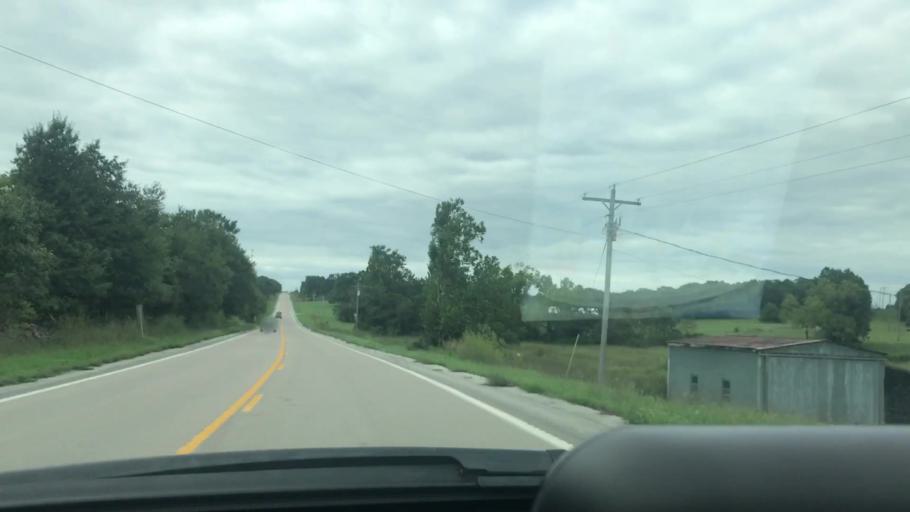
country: US
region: Missouri
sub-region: Benton County
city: Warsaw
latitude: 38.1337
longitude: -93.2809
